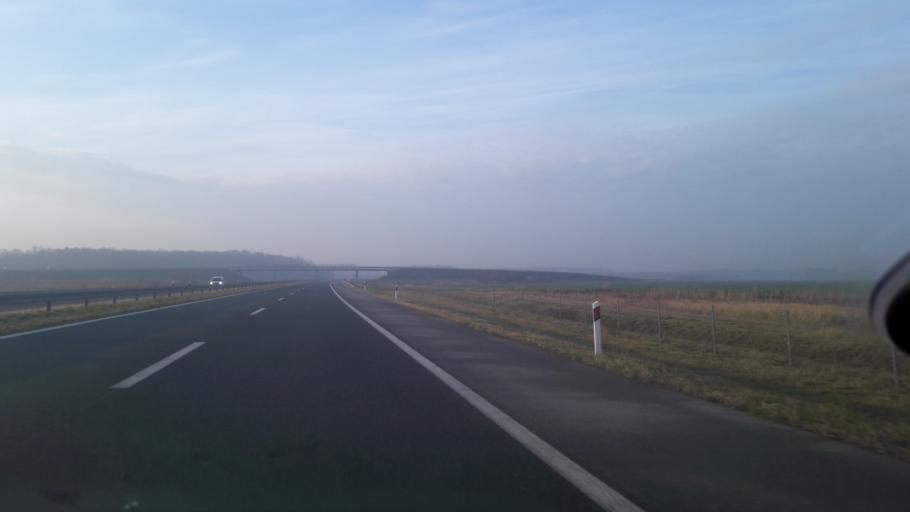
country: HR
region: Osjecko-Baranjska
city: Vuka
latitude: 45.4849
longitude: 18.4955
